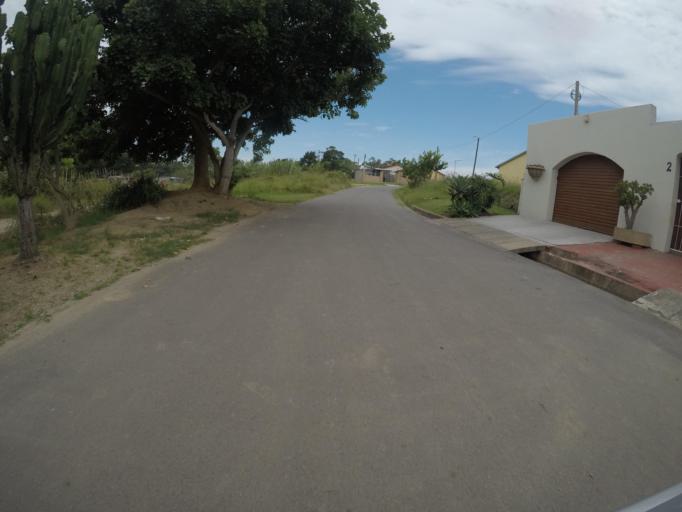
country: ZA
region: Eastern Cape
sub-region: Buffalo City Metropolitan Municipality
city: East London
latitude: -32.9924
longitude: 27.8807
